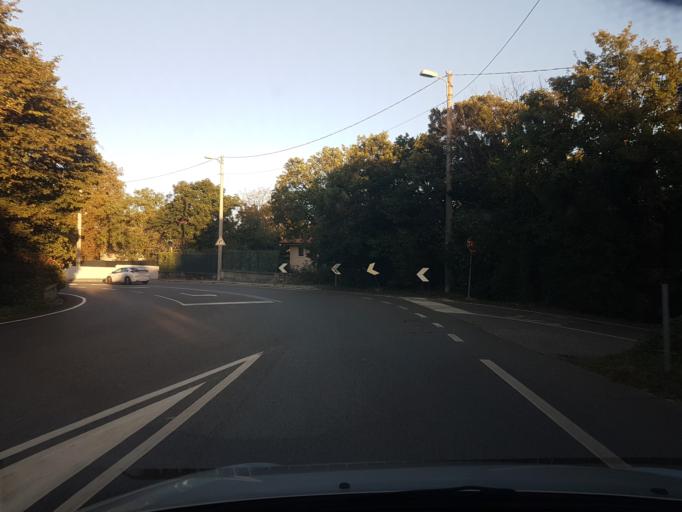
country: IT
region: Friuli Venezia Giulia
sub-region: Provincia di Trieste
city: Villa Opicina
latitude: 45.6916
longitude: 13.7852
